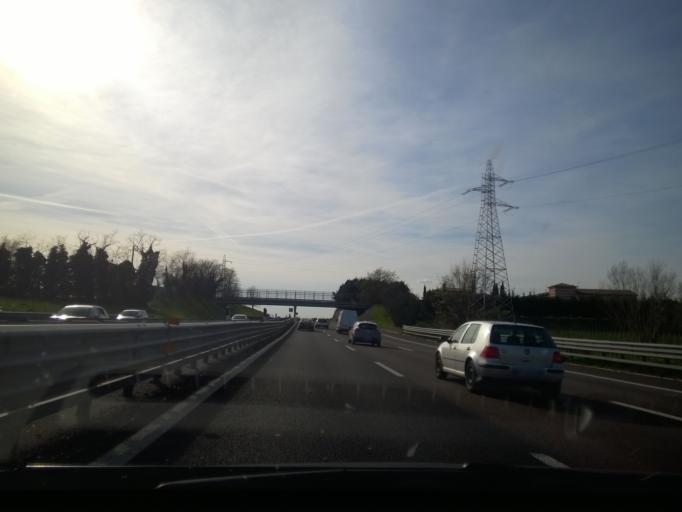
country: IT
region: Veneto
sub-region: Provincia di Verona
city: Peschiera del Garda
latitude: 45.4312
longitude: 10.6577
